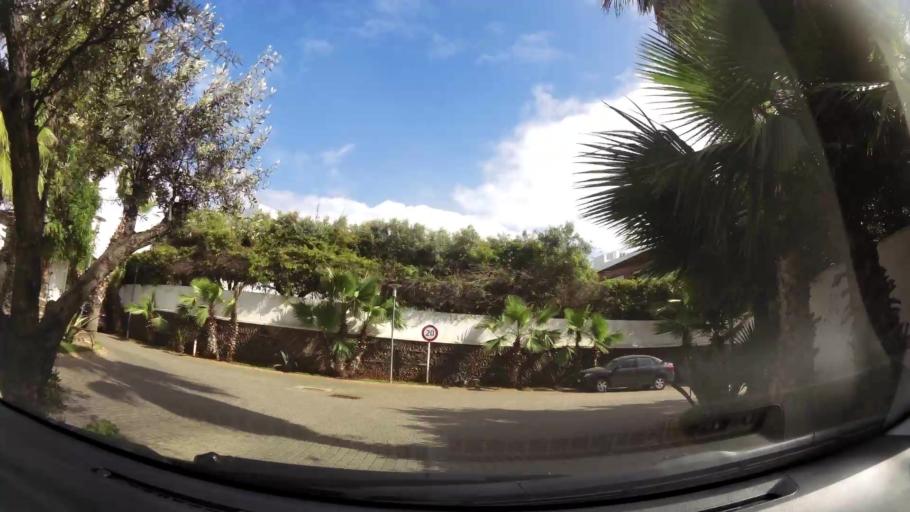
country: MA
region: Grand Casablanca
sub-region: Casablanca
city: Casablanca
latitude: 33.5691
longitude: -7.7059
